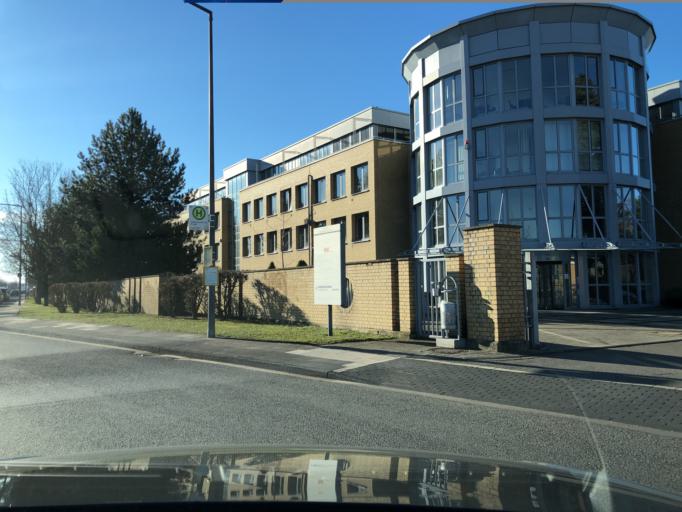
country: DE
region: North Rhine-Westphalia
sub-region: Regierungsbezirk Koln
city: Wahn-Heide
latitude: 50.8453
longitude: 7.1021
